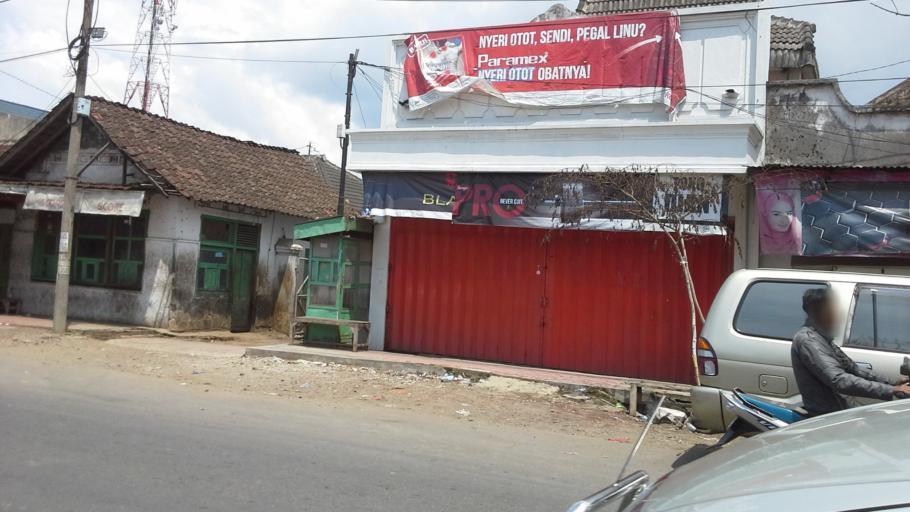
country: ID
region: East Java
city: Krajan Dua Sumbersari
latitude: -8.0308
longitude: 113.7764
